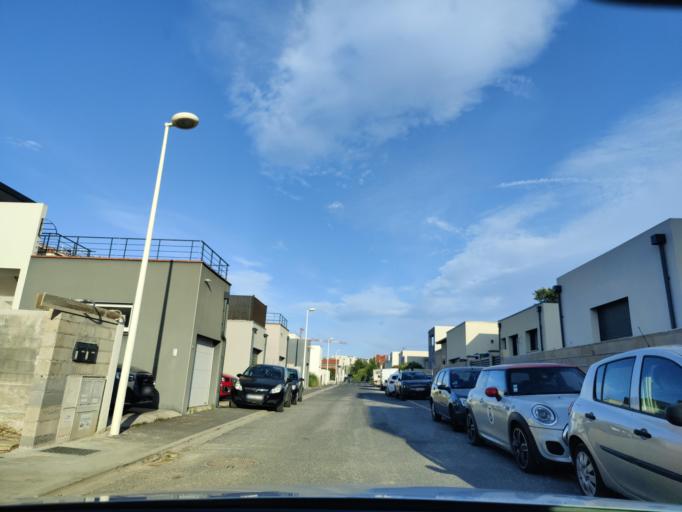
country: FR
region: Languedoc-Roussillon
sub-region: Departement des Pyrenees-Orientales
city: Perpignan
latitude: 42.6778
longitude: 2.8776
